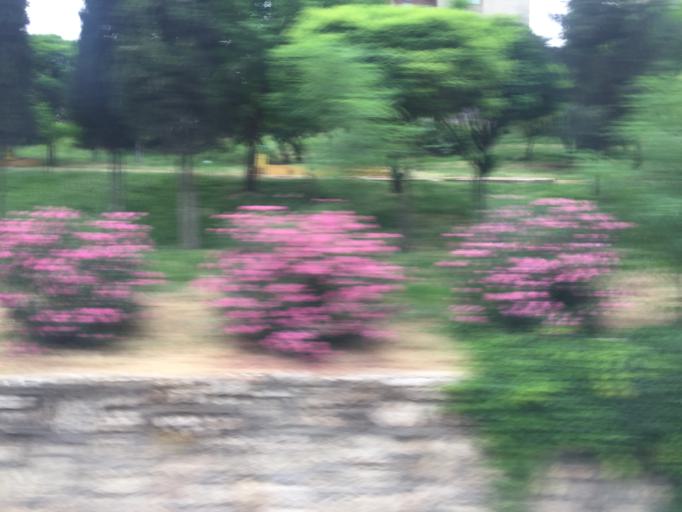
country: TR
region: Gaziantep
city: Gaziantep
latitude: 37.0546
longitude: 37.4172
